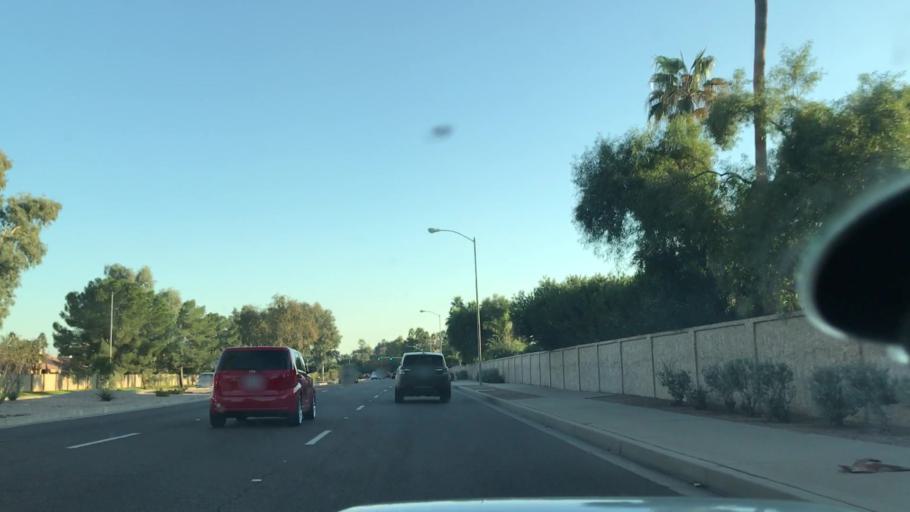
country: US
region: Arizona
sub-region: Maricopa County
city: Paradise Valley
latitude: 33.5694
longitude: -111.9039
